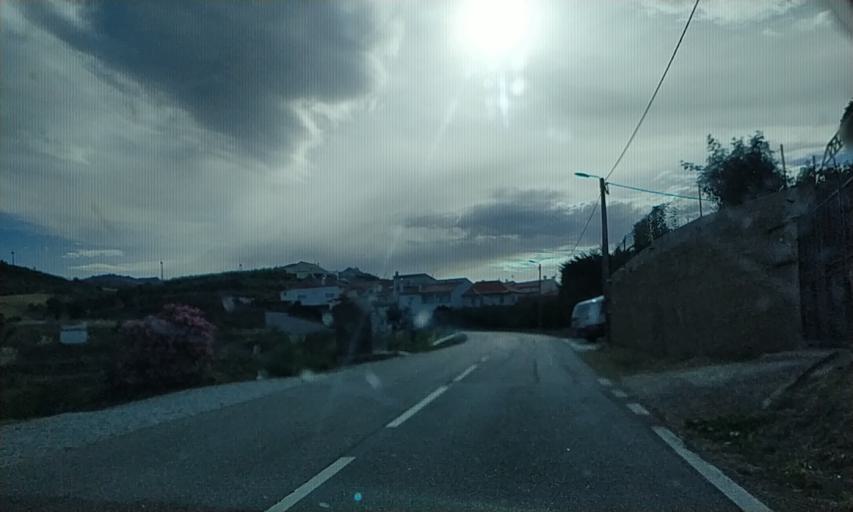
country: PT
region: Viseu
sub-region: Penedono
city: Penedono
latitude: 41.0682
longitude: -7.3949
